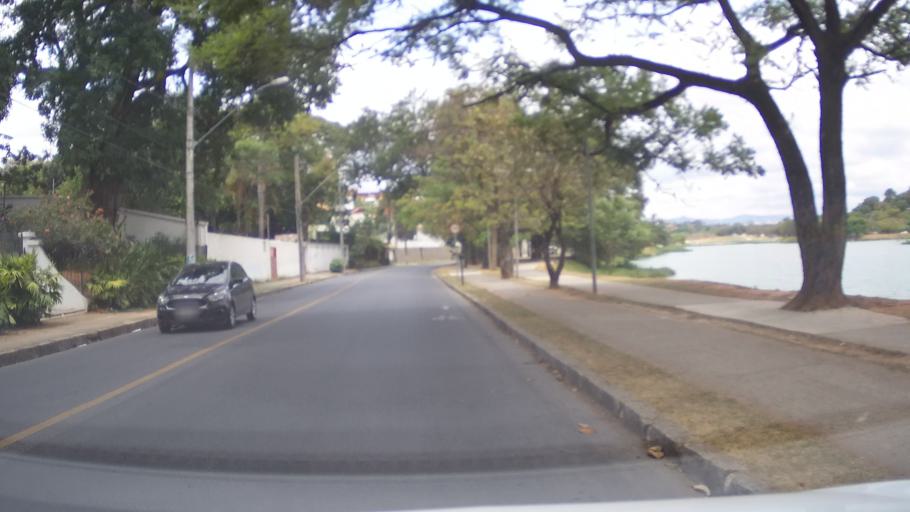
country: BR
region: Minas Gerais
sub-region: Belo Horizonte
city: Belo Horizonte
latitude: -19.8393
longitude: -43.9937
